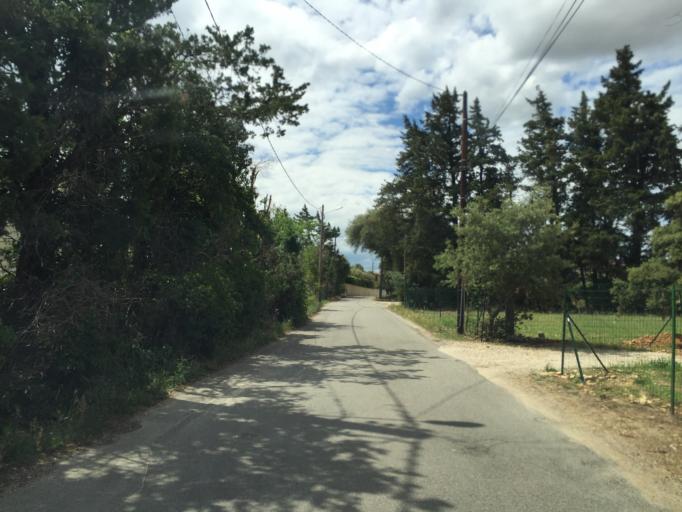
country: FR
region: Provence-Alpes-Cote d'Azur
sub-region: Departement du Vaucluse
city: Sorgues
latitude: 44.0199
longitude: 4.8612
